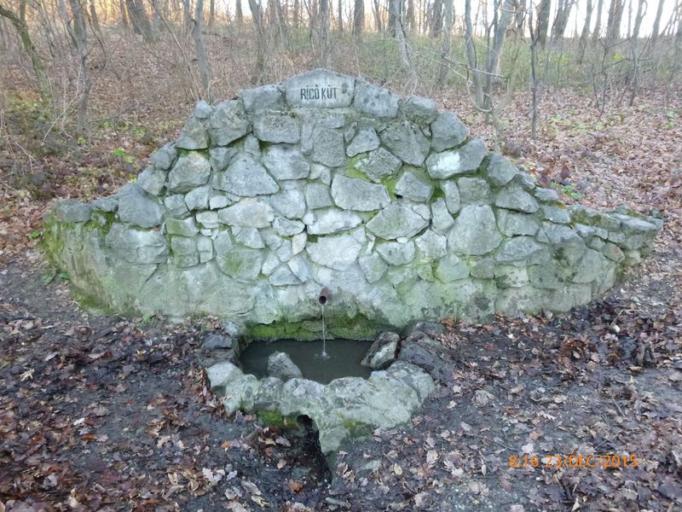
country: HU
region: Baranya
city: Pecs
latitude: 46.1302
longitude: 18.2511
